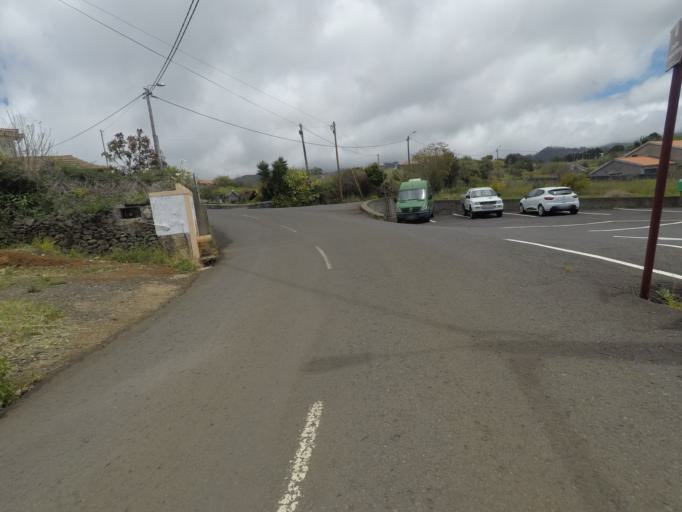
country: PT
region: Madeira
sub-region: Calheta
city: Faja da Ovelha
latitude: 32.7528
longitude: -17.2144
